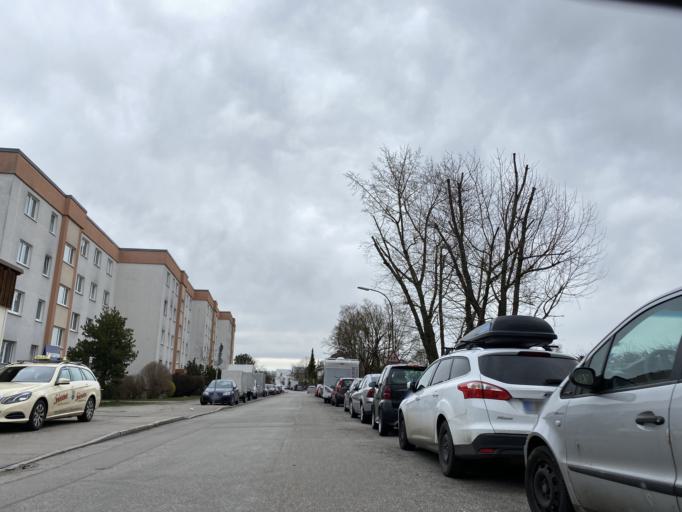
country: DE
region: Bavaria
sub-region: Upper Bavaria
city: Fuerstenfeldbruck
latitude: 48.1807
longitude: 11.2418
